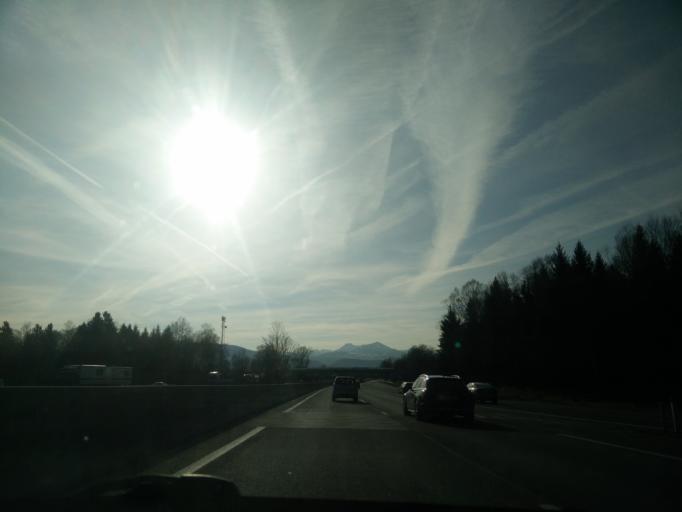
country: AT
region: Salzburg
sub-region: Politischer Bezirk Salzburg-Umgebung
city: Grodig
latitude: 47.7691
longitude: 12.9862
